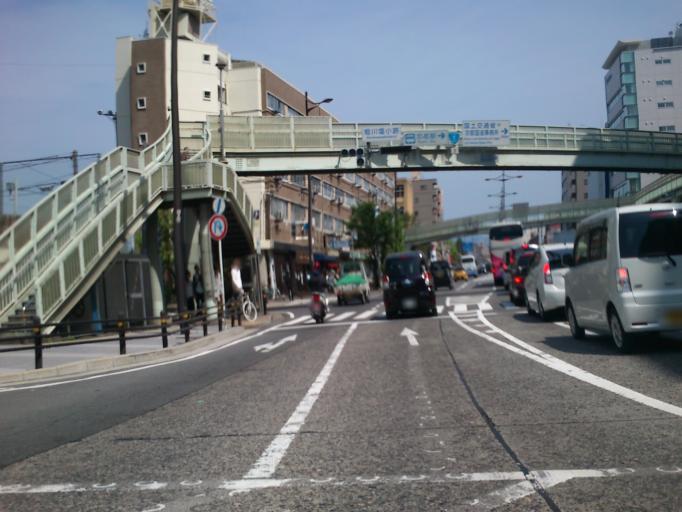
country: JP
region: Kyoto
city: Kyoto
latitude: 34.9864
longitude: 135.7531
